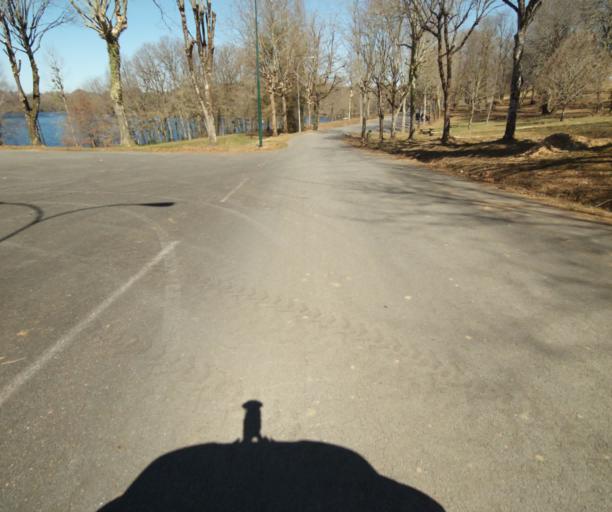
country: FR
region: Limousin
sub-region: Departement de la Correze
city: Seilhac
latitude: 45.3776
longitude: 1.6997
